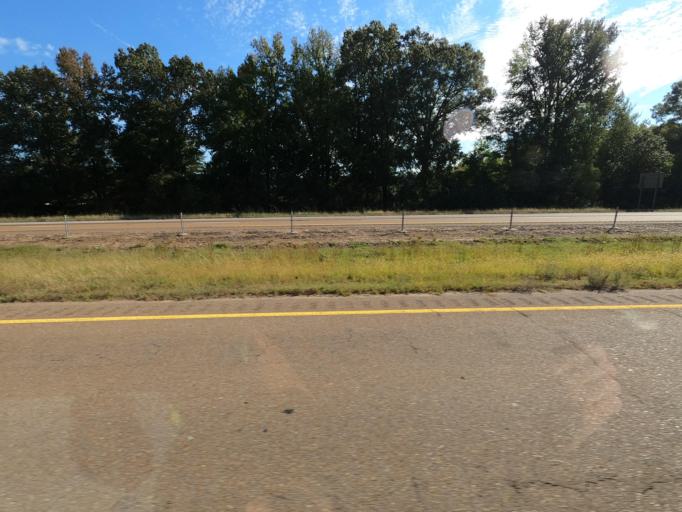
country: US
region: Tennessee
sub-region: Shelby County
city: Arlington
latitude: 35.2644
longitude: -89.6790
